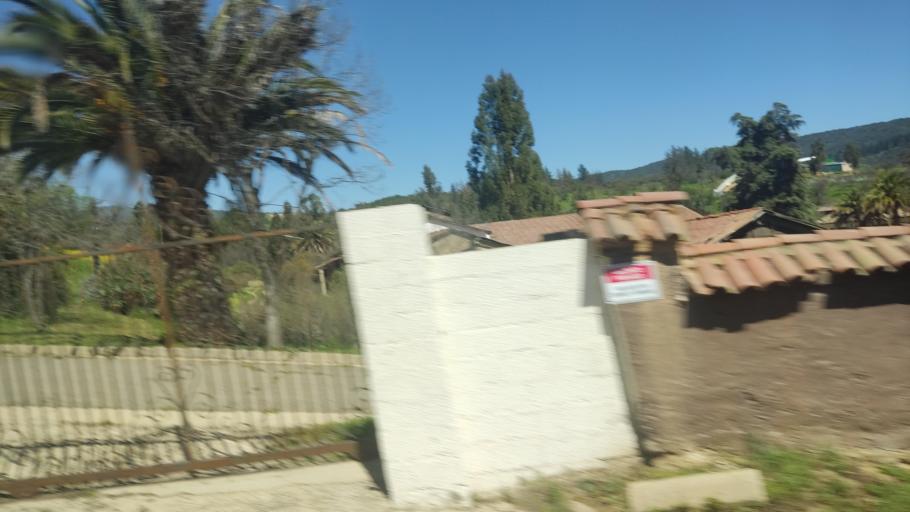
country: CL
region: Valparaiso
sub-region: Provincia de Marga Marga
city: Villa Alemana
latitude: -33.1531
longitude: -71.3336
